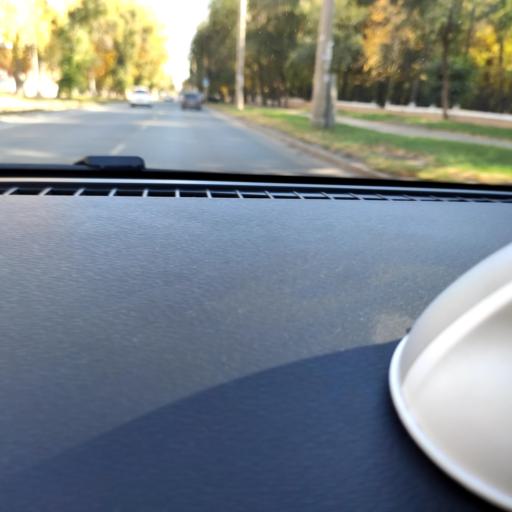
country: RU
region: Samara
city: Samara
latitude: 53.2243
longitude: 50.2377
